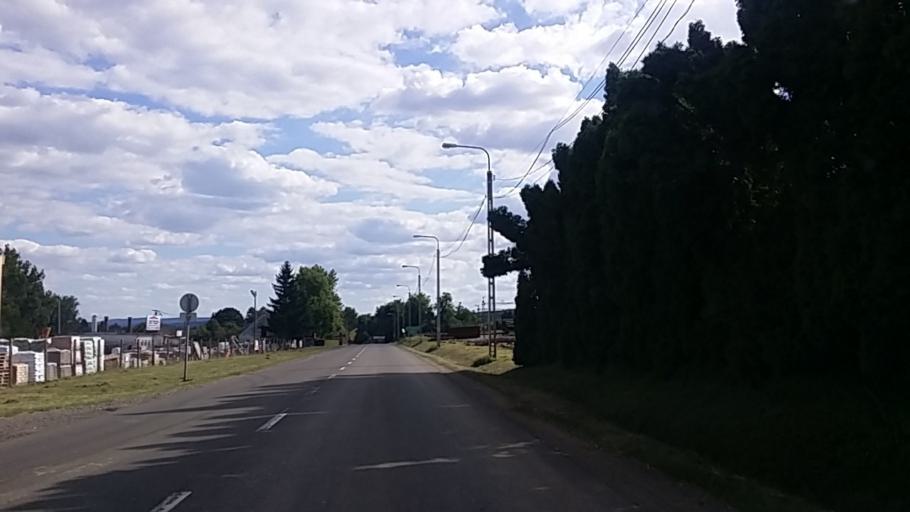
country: HU
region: Baranya
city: Sasd
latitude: 46.2618
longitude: 18.1059
